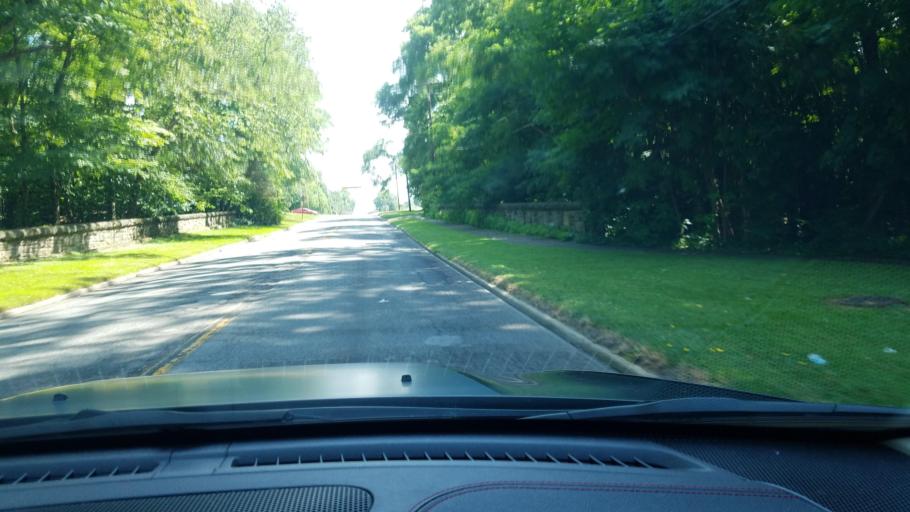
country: US
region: Ohio
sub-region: Mahoning County
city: Youngstown
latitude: 41.0785
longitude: -80.6998
